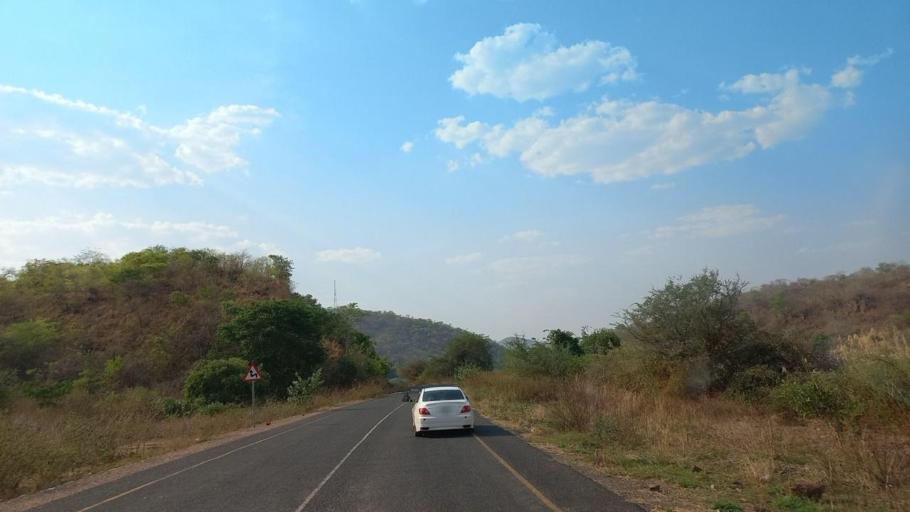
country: ZM
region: Lusaka
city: Luangwa
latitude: -15.0131
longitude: 30.2202
